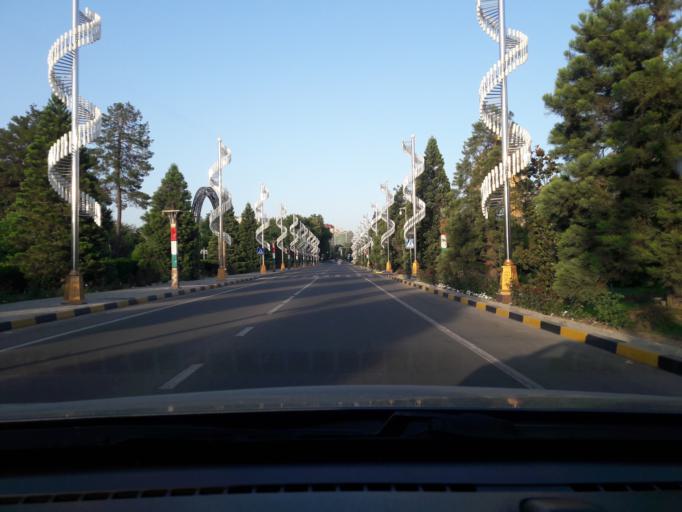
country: TJ
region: Dushanbe
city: Dushanbe
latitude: 38.5745
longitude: 68.7831
